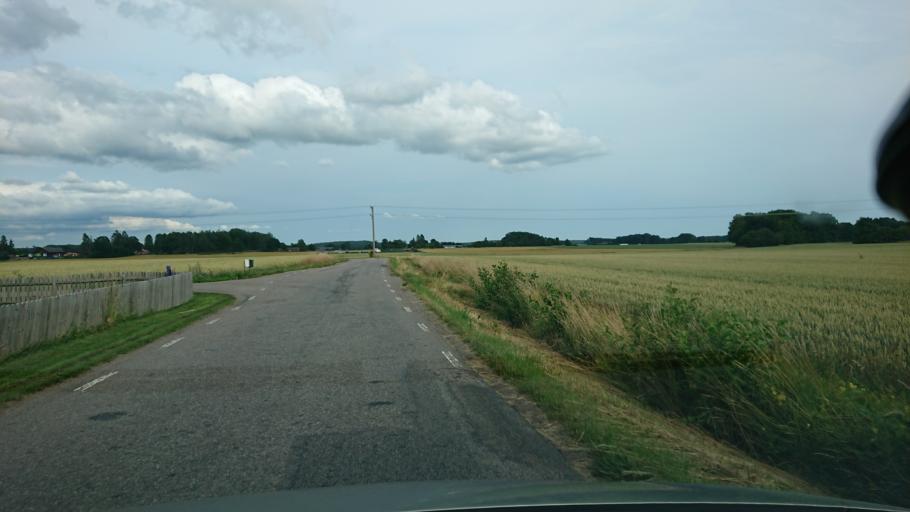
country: SE
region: Uppsala
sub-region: Osthammars Kommun
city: Bjorklinge
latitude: 59.9906
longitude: 17.5119
